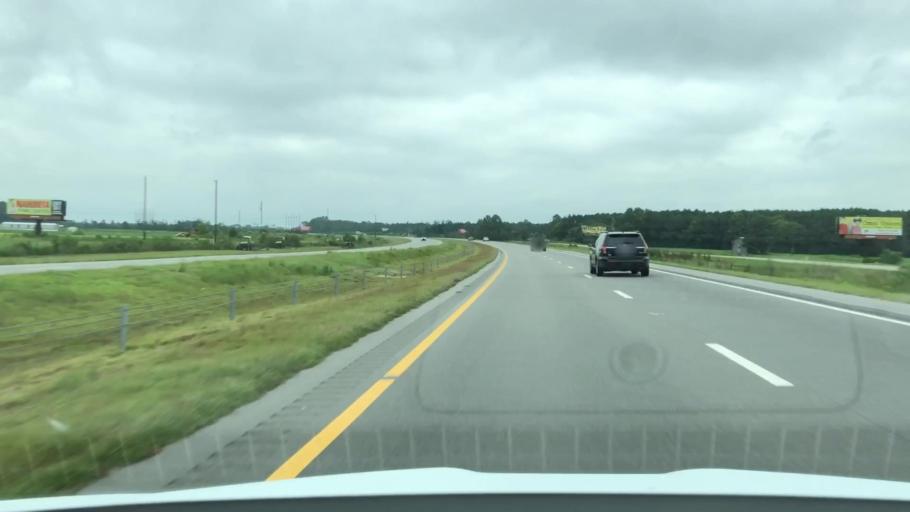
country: US
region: North Carolina
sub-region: Wayne County
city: Elroy
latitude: 35.3926
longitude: -77.8668
